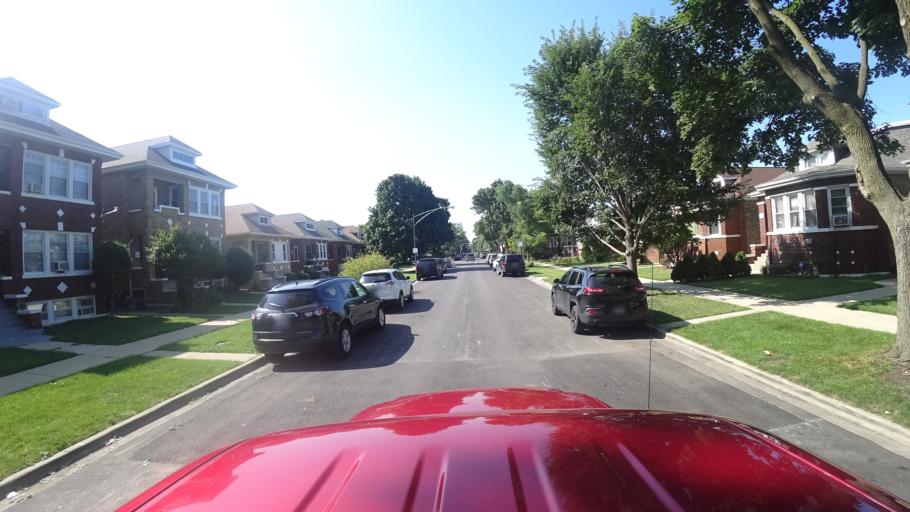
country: US
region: Illinois
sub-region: Cook County
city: Chicago
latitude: 41.7927
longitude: -87.6913
